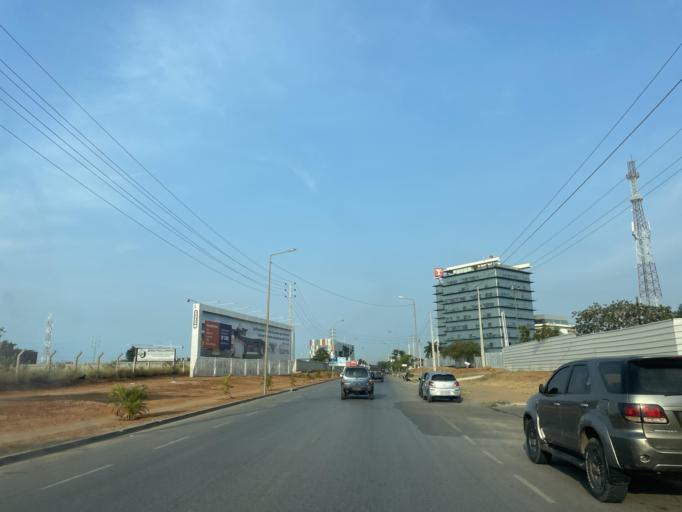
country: AO
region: Luanda
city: Luanda
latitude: -8.9189
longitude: 13.1927
